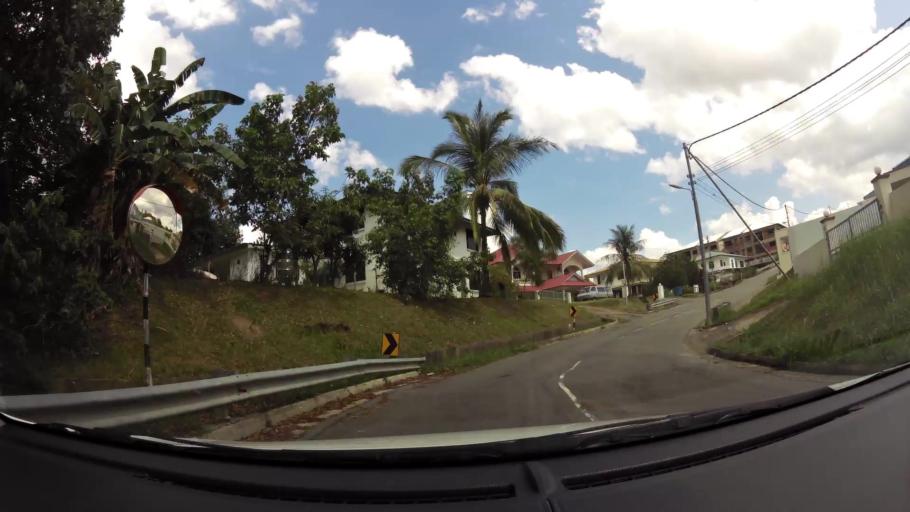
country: BN
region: Brunei and Muara
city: Bandar Seri Begawan
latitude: 4.9419
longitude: 114.9669
